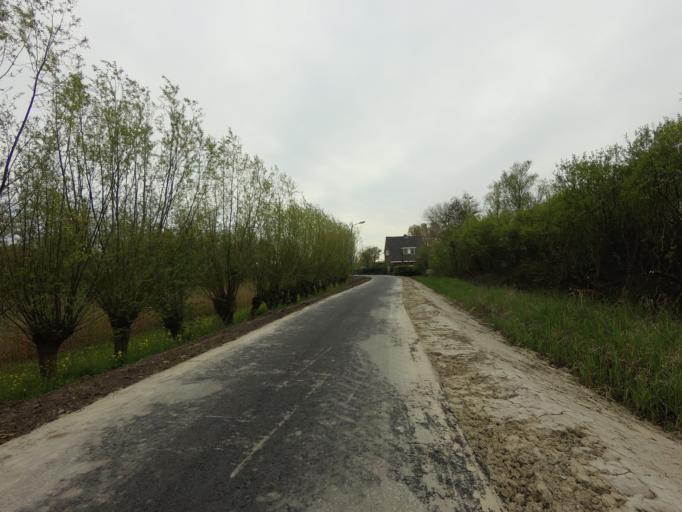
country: NL
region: North Holland
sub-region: Gemeente Diemen
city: Diemen
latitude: 52.3349
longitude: 4.9802
